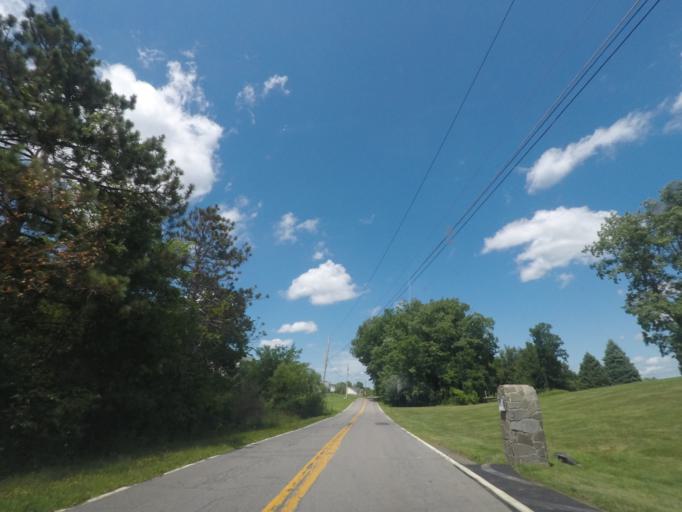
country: US
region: New York
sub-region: Schenectady County
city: Rotterdam
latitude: 42.7197
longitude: -73.9595
